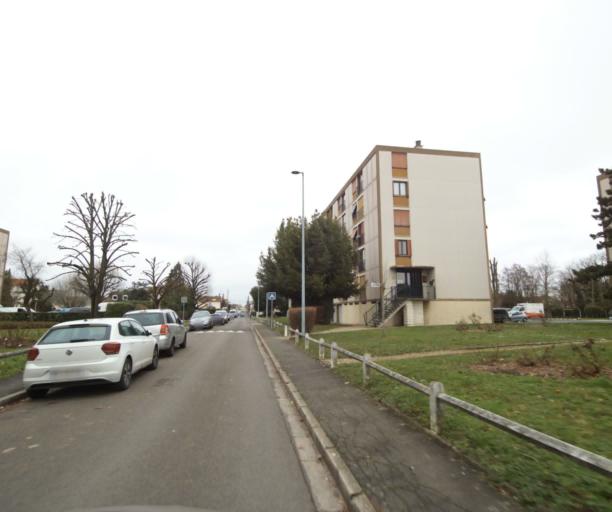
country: FR
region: Ile-de-France
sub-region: Departement du Val-de-Marne
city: Ablon-sur-Seine
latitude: 48.7256
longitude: 2.4330
